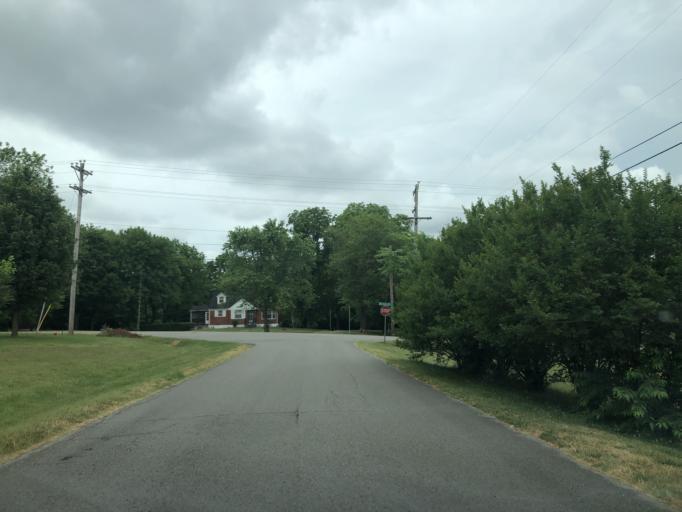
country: US
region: Tennessee
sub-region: Davidson County
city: Goodlettsville
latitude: 36.2641
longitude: -86.7621
